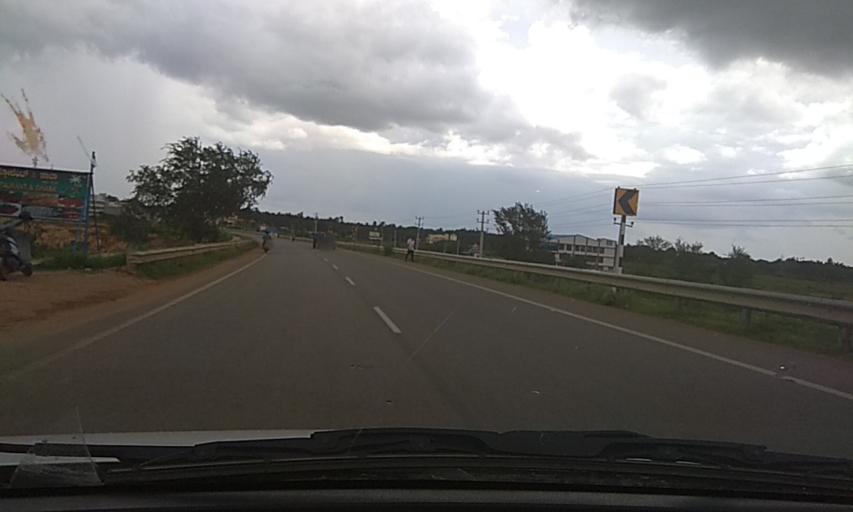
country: IN
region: Karnataka
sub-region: Tumkur
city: Kunigal
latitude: 13.1627
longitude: 77.0310
